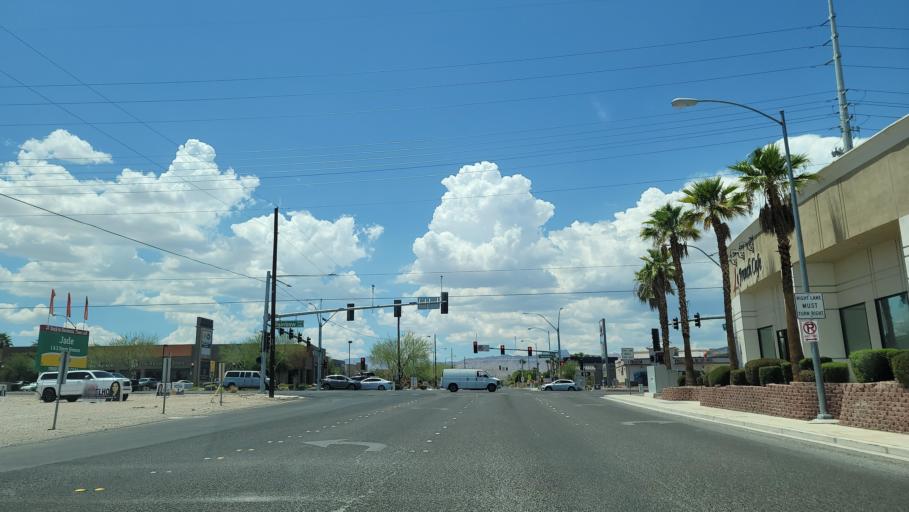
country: US
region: Nevada
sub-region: Clark County
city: Spring Valley
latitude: 36.0779
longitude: -115.2418
